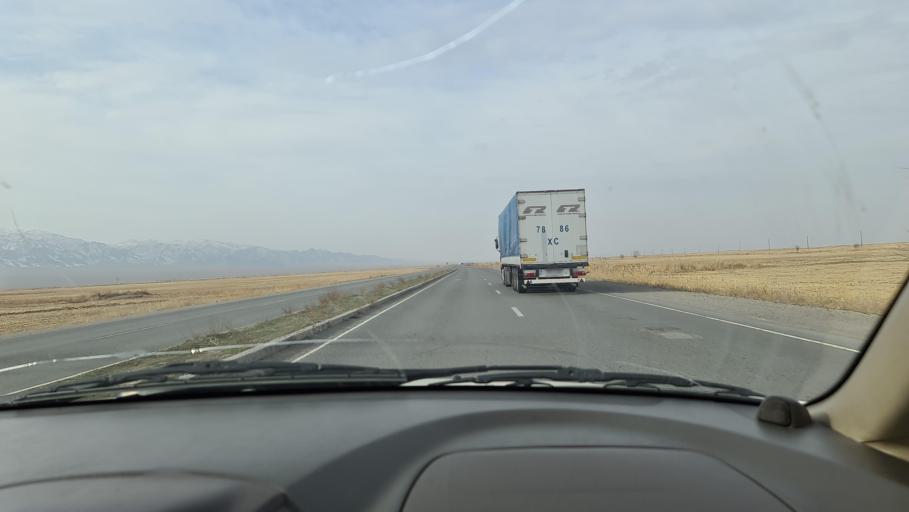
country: KG
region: Chuy
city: Tokmok
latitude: 43.3511
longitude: 75.4671
